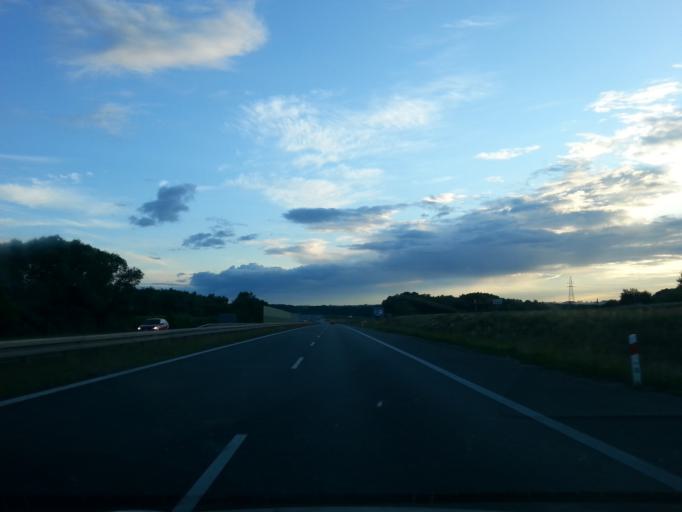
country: PL
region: Lower Silesian Voivodeship
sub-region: Powiat olesnicki
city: Sycow
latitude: 51.2992
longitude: 17.7578
